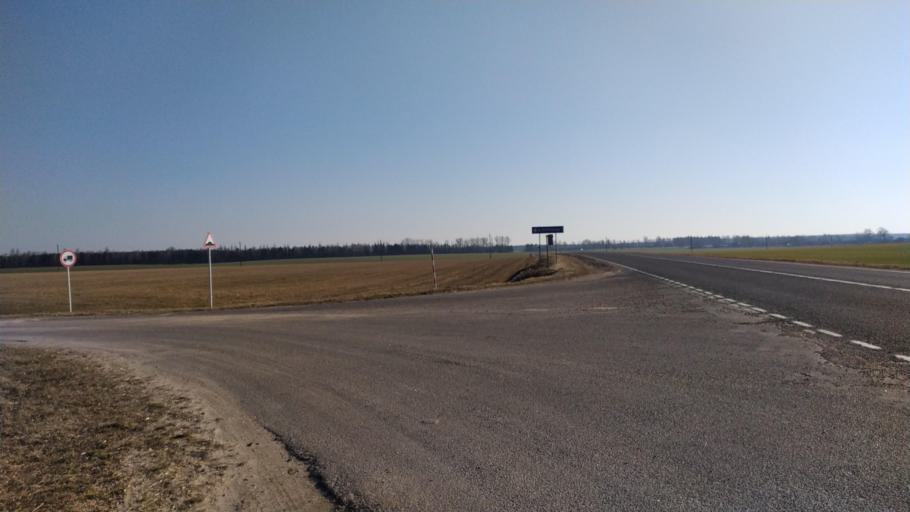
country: BY
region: Brest
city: Kamyanyets
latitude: 52.3815
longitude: 23.7886
